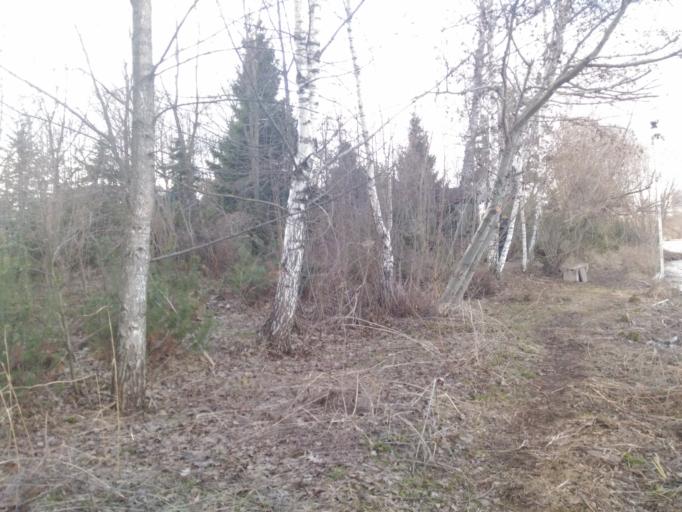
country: RU
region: Moscow
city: Strogino
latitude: 55.7898
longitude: 37.4174
